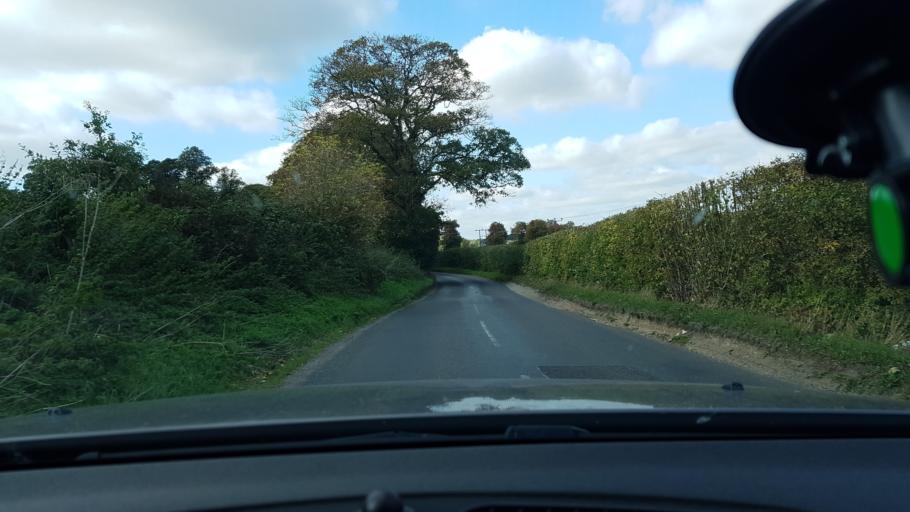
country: GB
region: England
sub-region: West Berkshire
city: Kintbury
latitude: 51.4057
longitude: -1.4765
